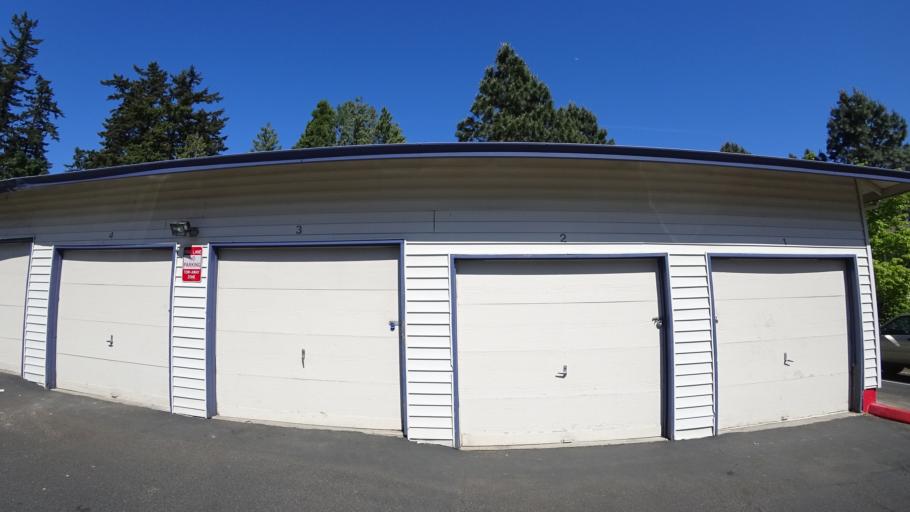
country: US
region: Oregon
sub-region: Multnomah County
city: Gresham
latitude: 45.4892
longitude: -122.4784
